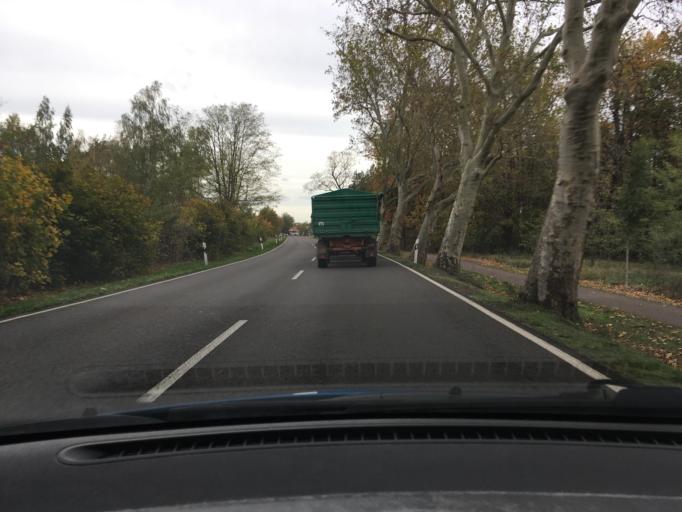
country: DE
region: Saxony-Anhalt
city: Wahlitz
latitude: 52.1008
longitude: 11.7843
